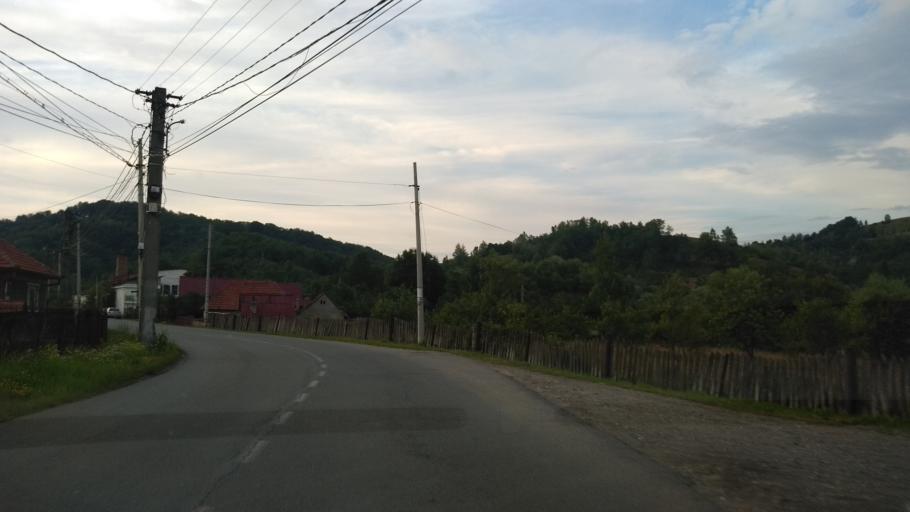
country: RO
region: Hunedoara
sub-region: Comuna Aninoasa
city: Iscroni
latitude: 45.3820
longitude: 23.3293
